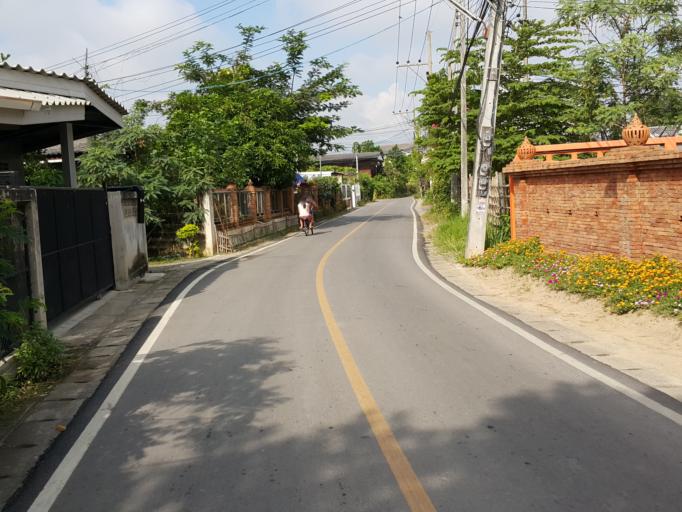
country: TH
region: Chiang Mai
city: San Kamphaeng
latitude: 18.7534
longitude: 99.0752
